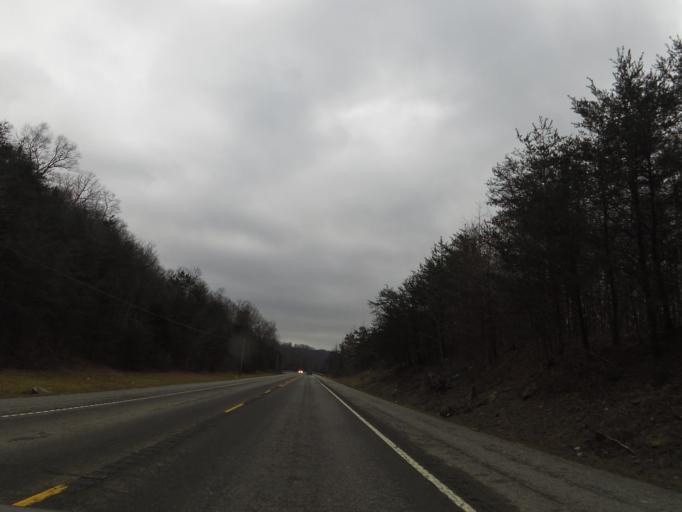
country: US
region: Tennessee
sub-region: Campbell County
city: Caryville
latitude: 36.3989
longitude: -84.2827
